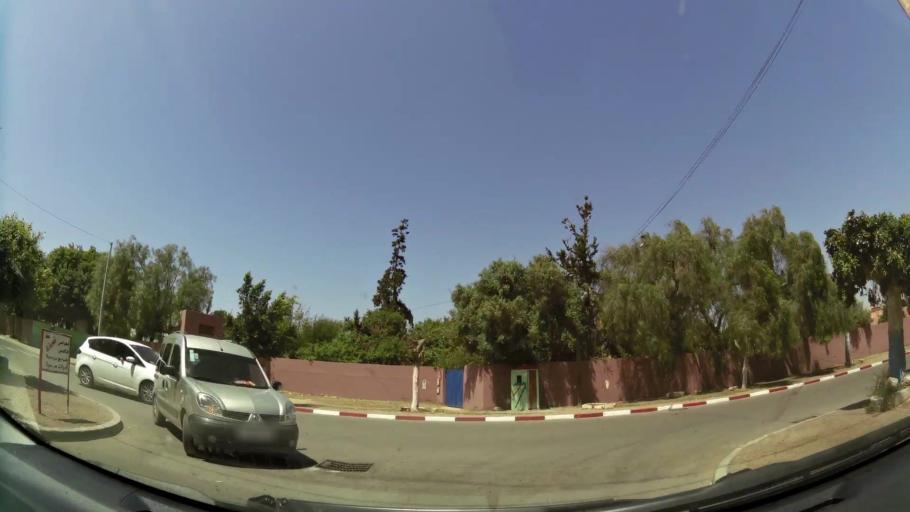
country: MA
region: Souss-Massa-Draa
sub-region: Inezgane-Ait Mellou
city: Inezgane
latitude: 30.3471
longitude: -9.4859
